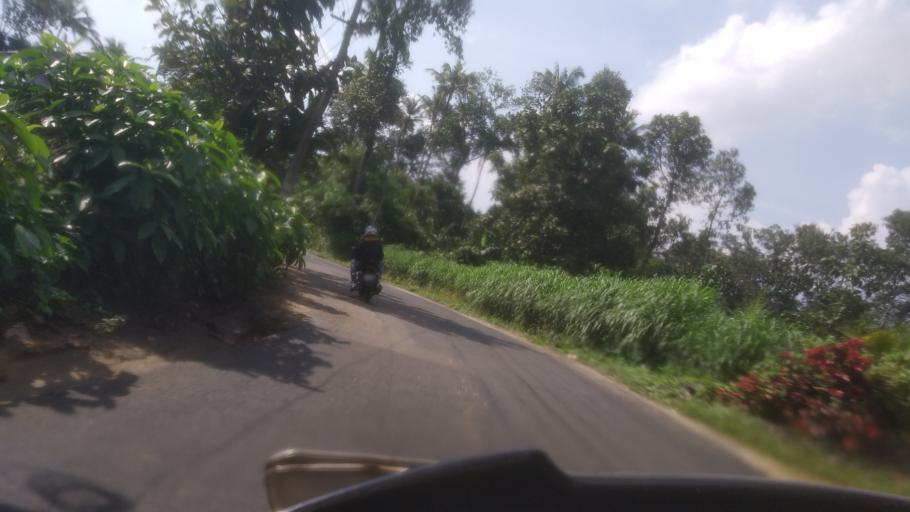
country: IN
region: Kerala
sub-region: Ernakulam
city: Kotamangalam
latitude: 10.0052
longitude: 76.7174
